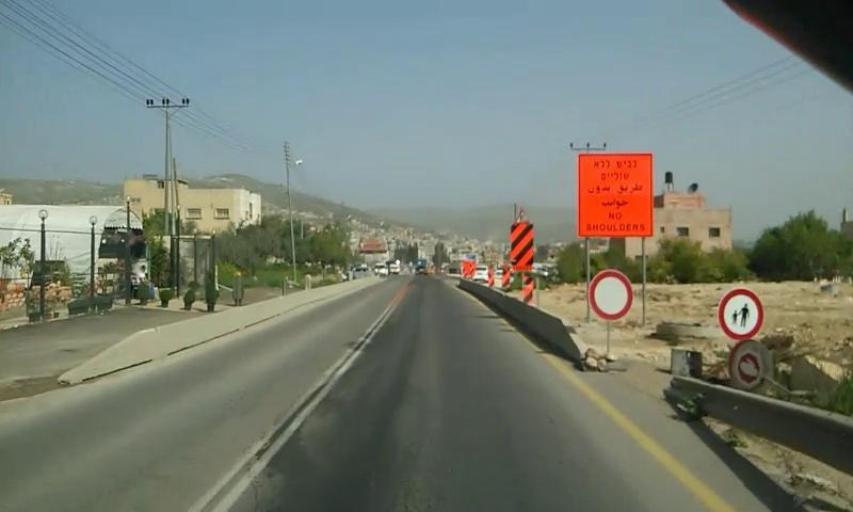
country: PS
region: West Bank
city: Huwwarah
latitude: 32.1358
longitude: 35.2582
